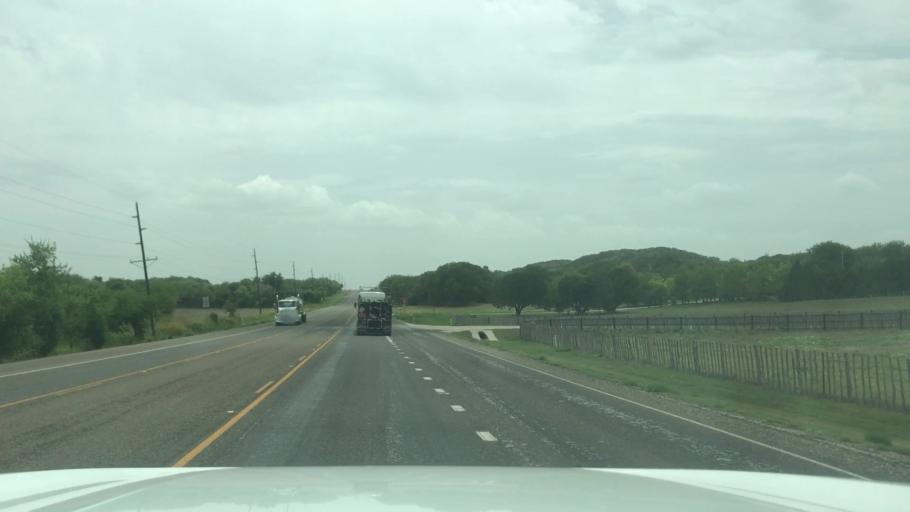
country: US
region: Texas
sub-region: Bosque County
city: Clifton
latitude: 31.7276
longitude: -97.5496
